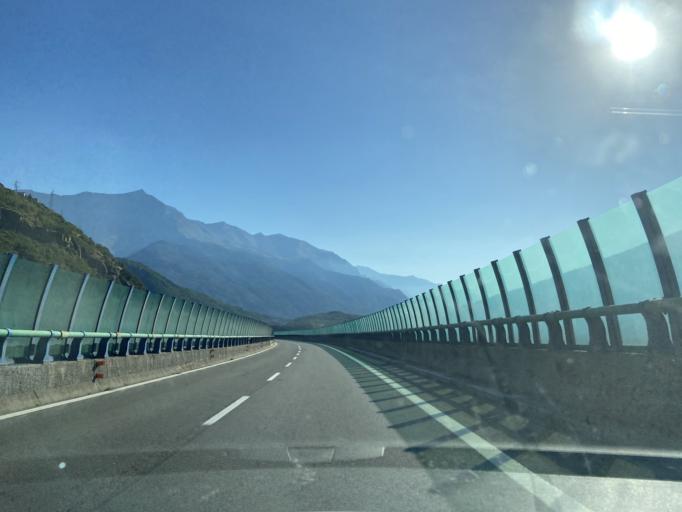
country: IT
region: Piedmont
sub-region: Provincia di Torino
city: Chiomonte
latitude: 45.1170
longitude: 6.9691
